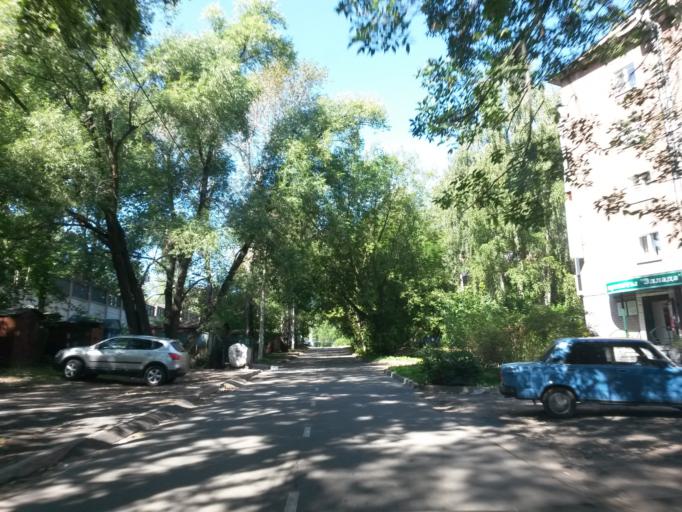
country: RU
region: Jaroslavl
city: Yaroslavl
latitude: 57.5876
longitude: 39.8622
